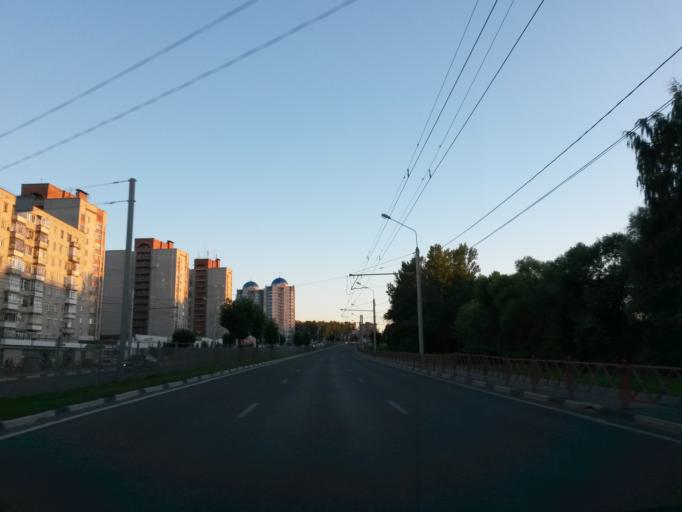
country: RU
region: Jaroslavl
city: Yaroslavl
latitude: 57.5846
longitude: 39.8551
